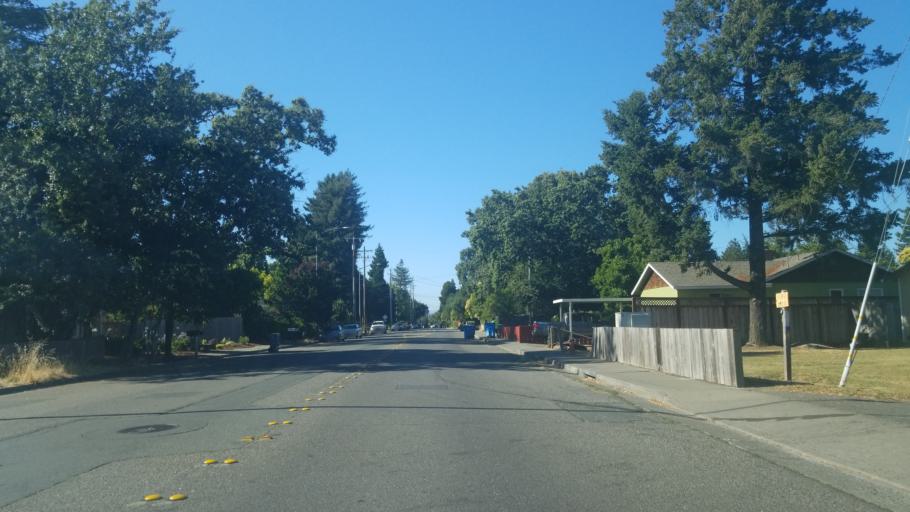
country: US
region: California
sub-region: Sonoma County
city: Roseland
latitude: 38.4205
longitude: -122.7242
